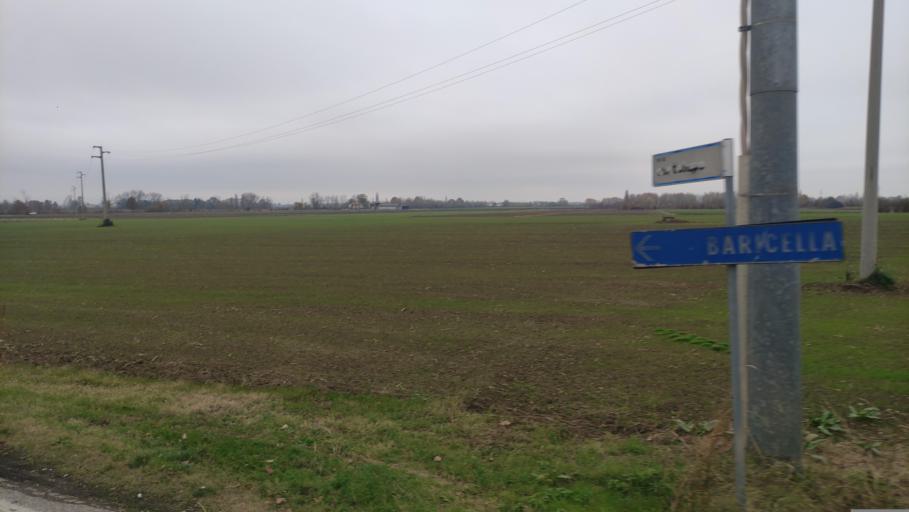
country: IT
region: Emilia-Romagna
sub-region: Provincia di Bologna
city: Baricella
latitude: 44.6140
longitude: 11.5302
